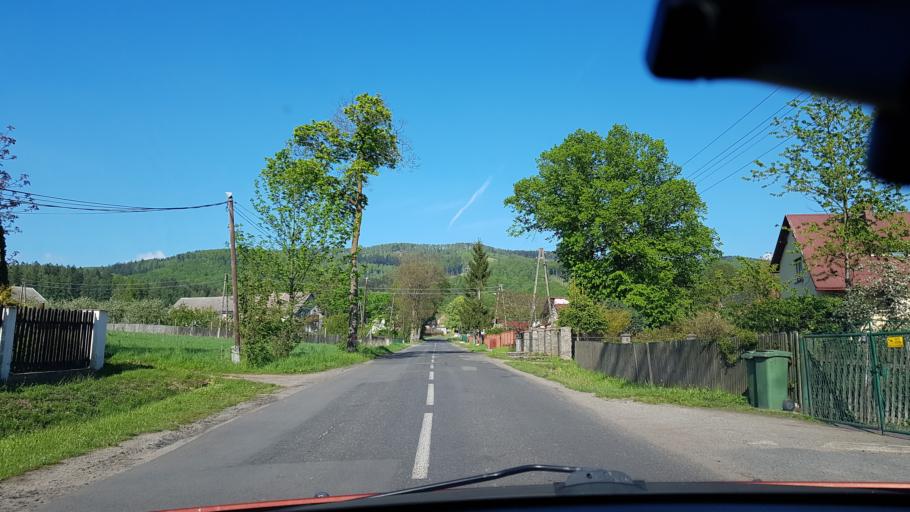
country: PL
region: Lower Silesian Voivodeship
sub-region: Powiat klodzki
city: Jugow
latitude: 50.5888
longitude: 16.5710
